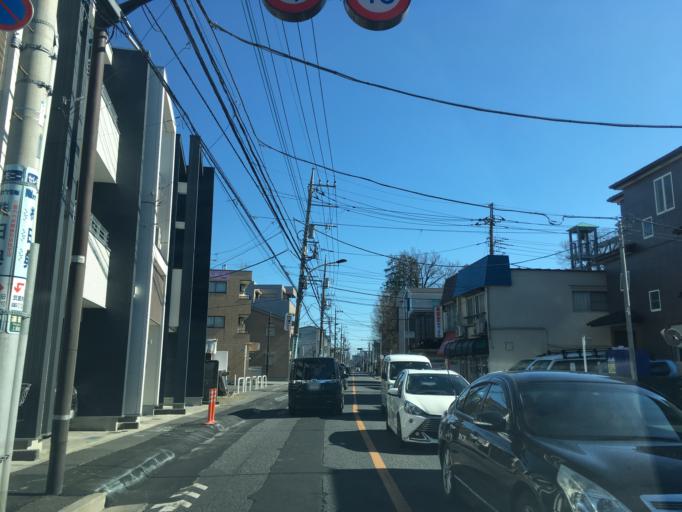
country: JP
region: Tokyo
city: Kamirenjaku
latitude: 35.6948
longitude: 139.5512
